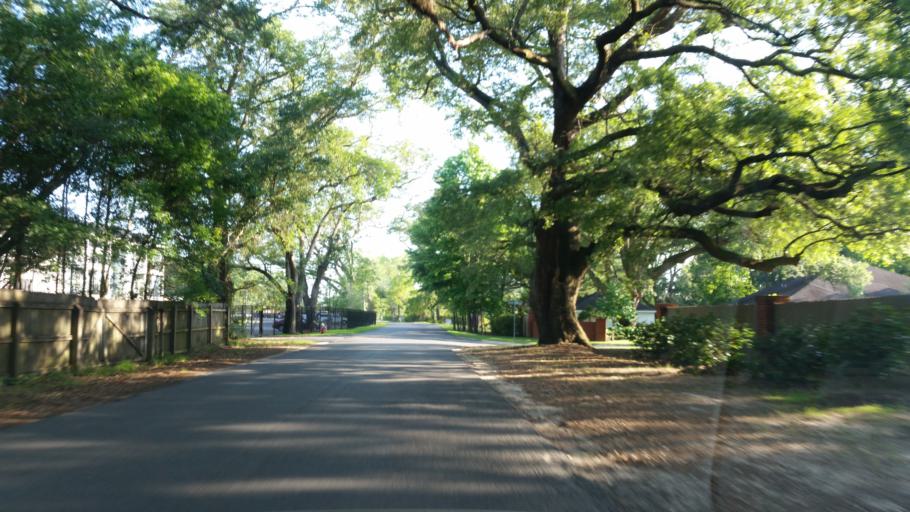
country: US
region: Florida
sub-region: Escambia County
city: Ferry Pass
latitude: 30.5377
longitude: -87.2159
